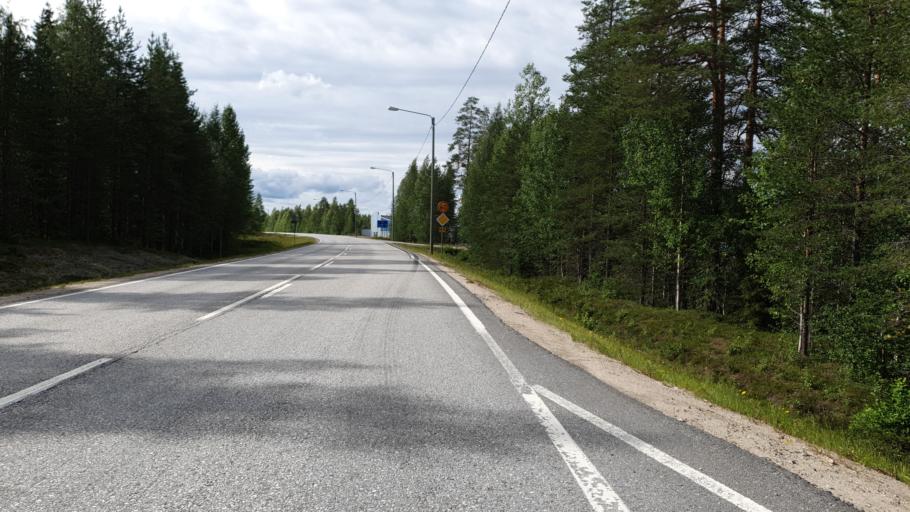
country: FI
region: Kainuu
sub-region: Kehys-Kainuu
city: Kuhmo
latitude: 64.5368
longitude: 29.9450
